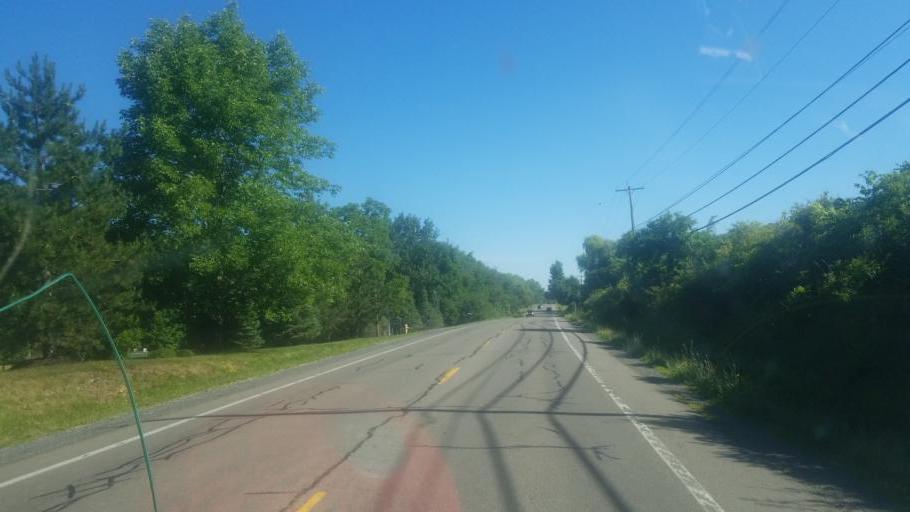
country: US
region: New York
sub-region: Ontario County
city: Canandaigua
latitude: 42.8421
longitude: -77.2558
